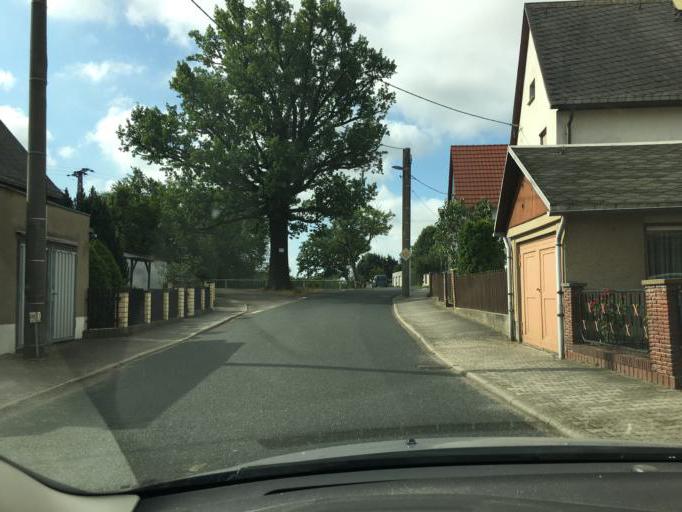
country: DE
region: Saxony
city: Frohburg
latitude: 51.0483
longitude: 12.6200
